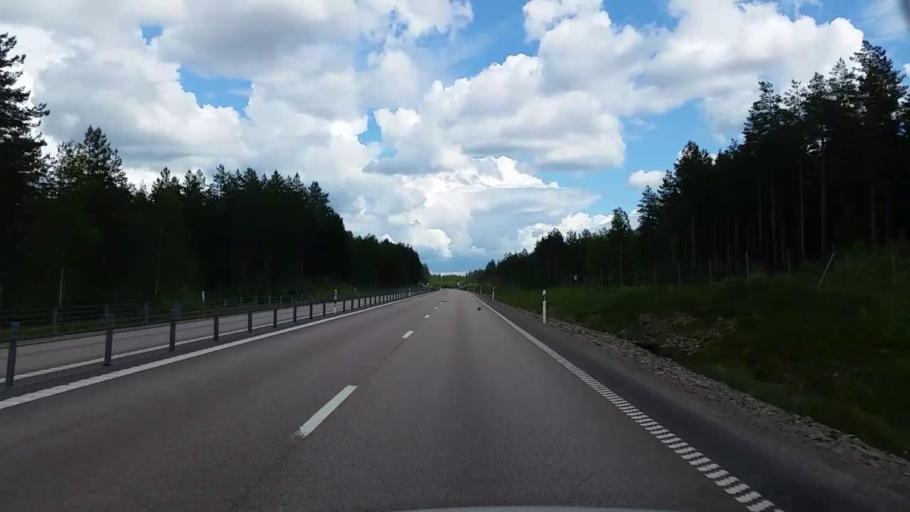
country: SE
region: Vaestmanland
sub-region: Norbergs Kommun
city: Norberg
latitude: 60.0785
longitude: 15.9761
